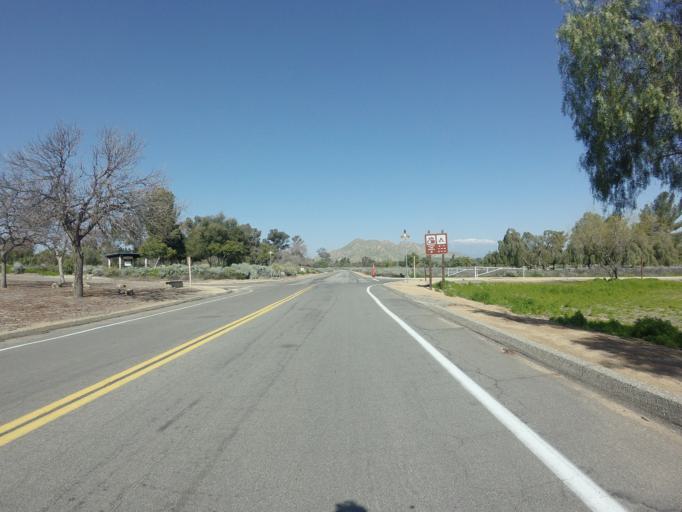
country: US
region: California
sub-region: Riverside County
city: Lakeview
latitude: 33.8727
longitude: -117.1775
